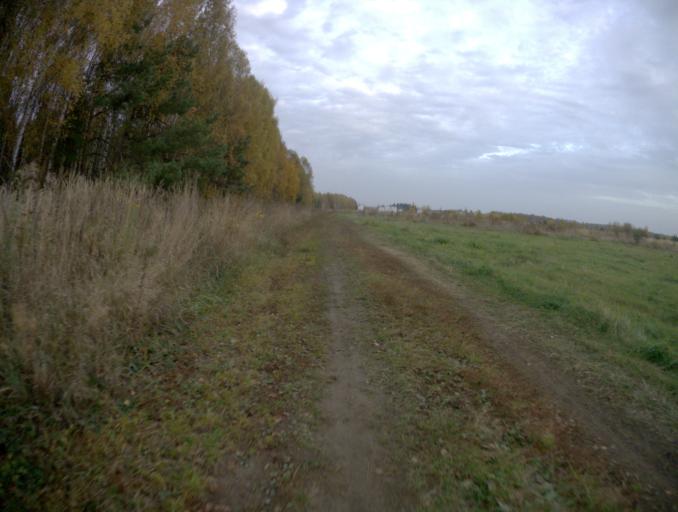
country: RU
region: Vladimir
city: Raduzhnyy
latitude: 56.0181
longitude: 40.3765
